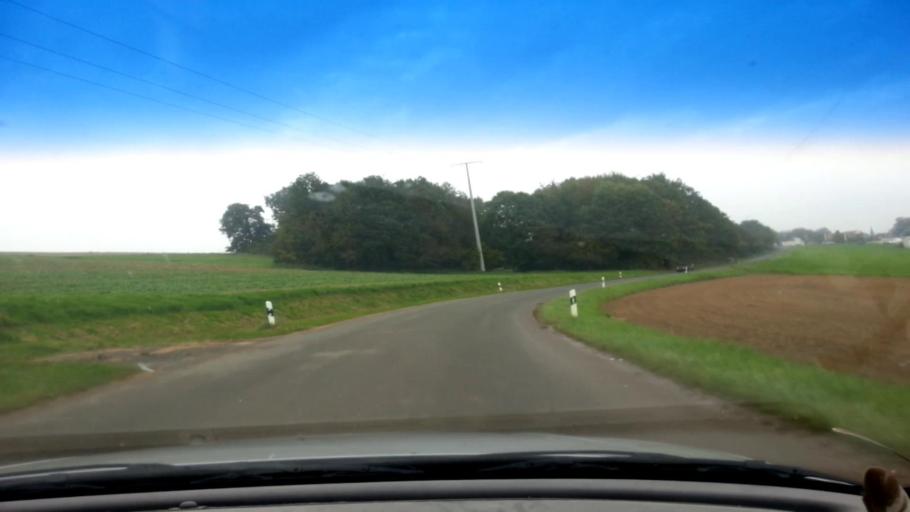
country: DE
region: Bavaria
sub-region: Upper Franconia
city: Rattelsdorf
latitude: 50.0624
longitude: 10.8965
